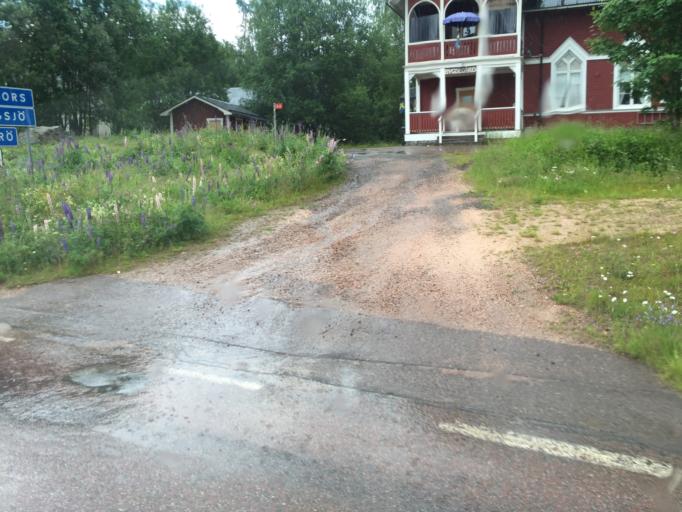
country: SE
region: Dalarna
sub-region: Malung-Saelens kommun
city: Malung
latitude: 60.5794
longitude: 13.8269
